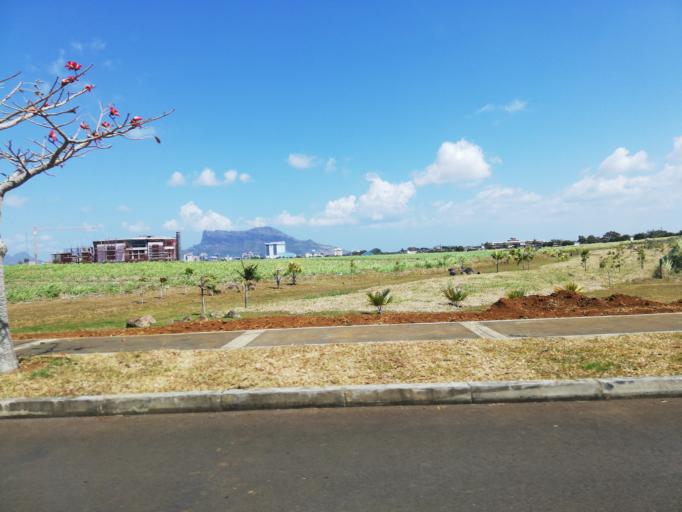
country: MU
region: Moka
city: Saint Pierre
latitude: -20.2294
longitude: 57.5114
